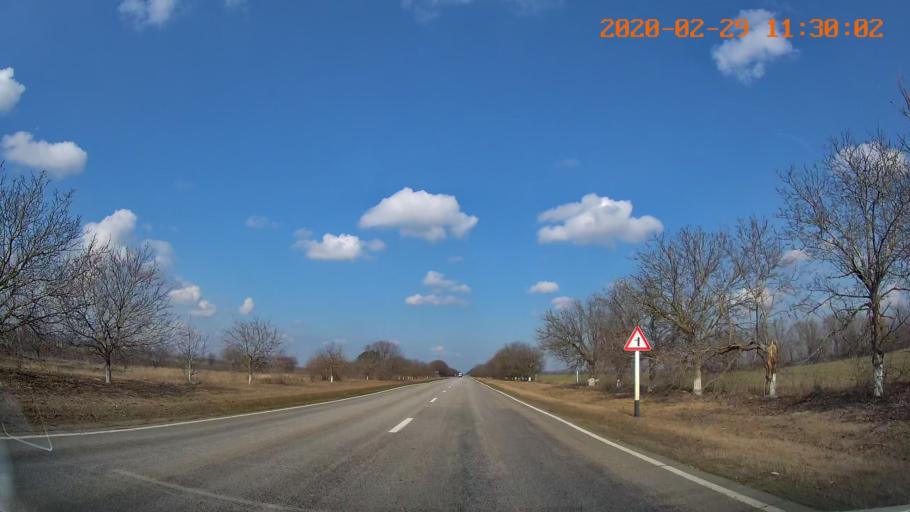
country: MD
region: Telenesti
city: Cocieri
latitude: 47.5036
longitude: 29.1194
